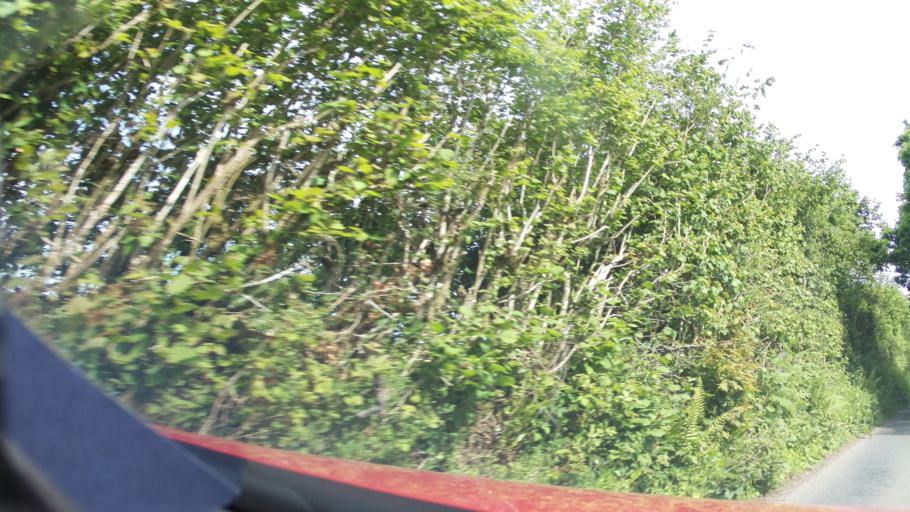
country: GB
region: England
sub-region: Devon
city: Kingsbridge
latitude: 50.3607
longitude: -3.7533
